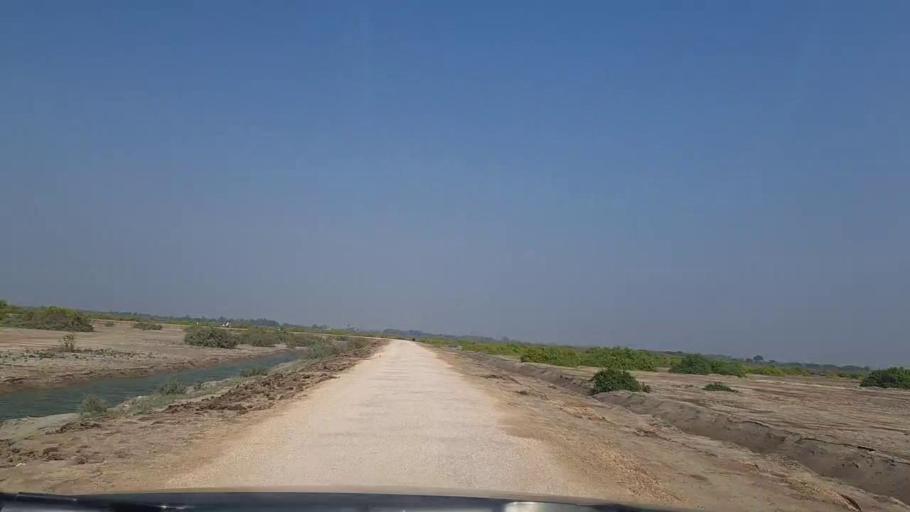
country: PK
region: Sindh
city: Mirpur Sakro
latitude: 24.5774
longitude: 67.7576
